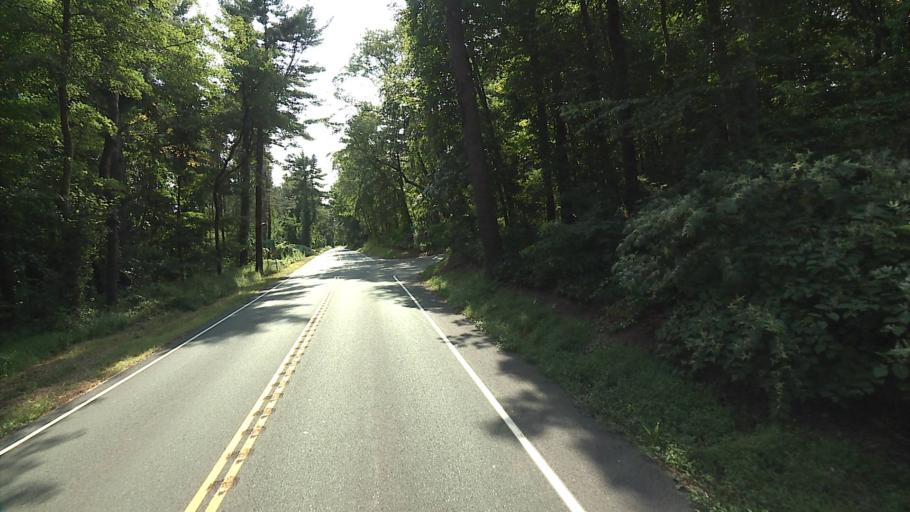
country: US
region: Connecticut
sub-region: Fairfield County
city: Southport
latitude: 41.2177
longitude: -73.2958
